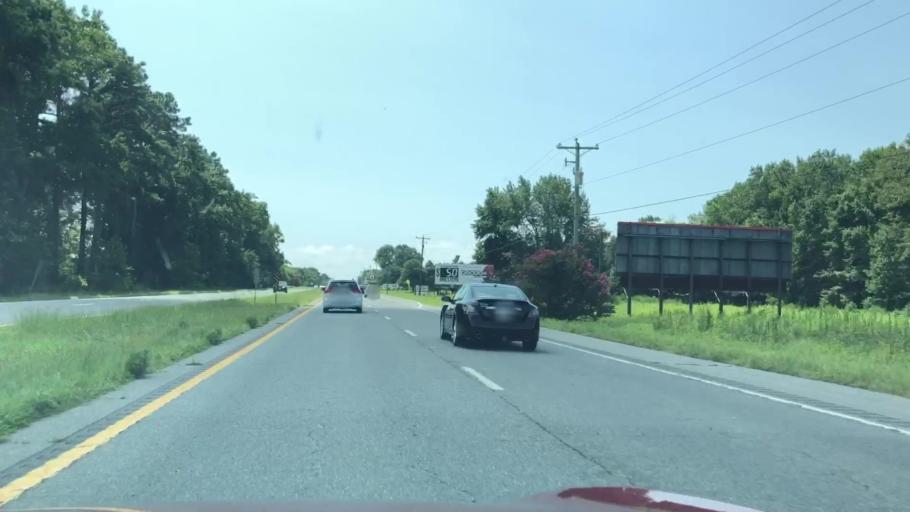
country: US
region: Virginia
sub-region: Northampton County
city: Cape Charles
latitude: 37.1926
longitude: -75.9678
